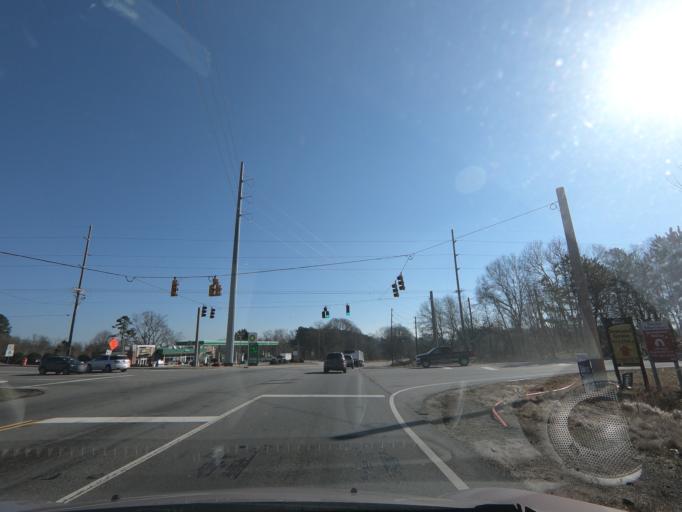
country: US
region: Georgia
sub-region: Forsyth County
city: Cumming
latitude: 34.2987
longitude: -84.1537
